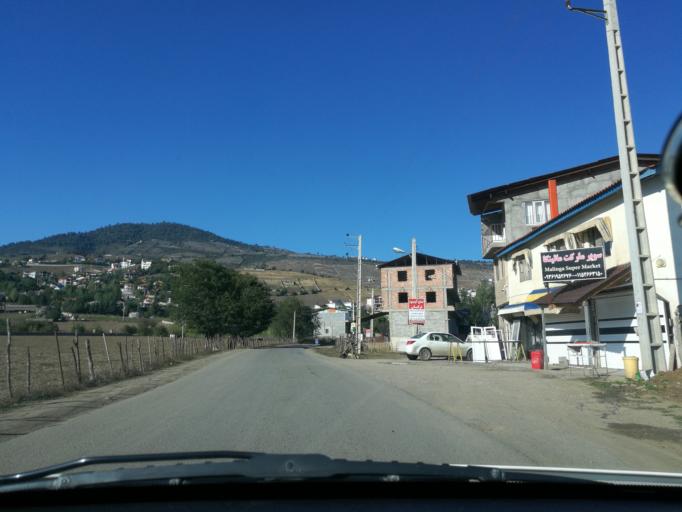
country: IR
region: Mazandaran
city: `Abbasabad
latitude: 36.5452
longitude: 51.1844
